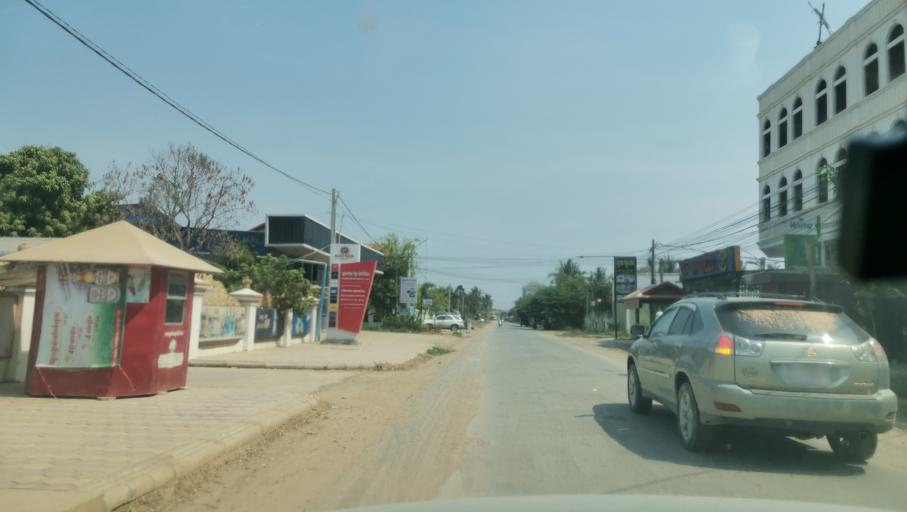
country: KH
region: Battambang
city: Battambang
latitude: 13.0987
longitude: 103.2035
